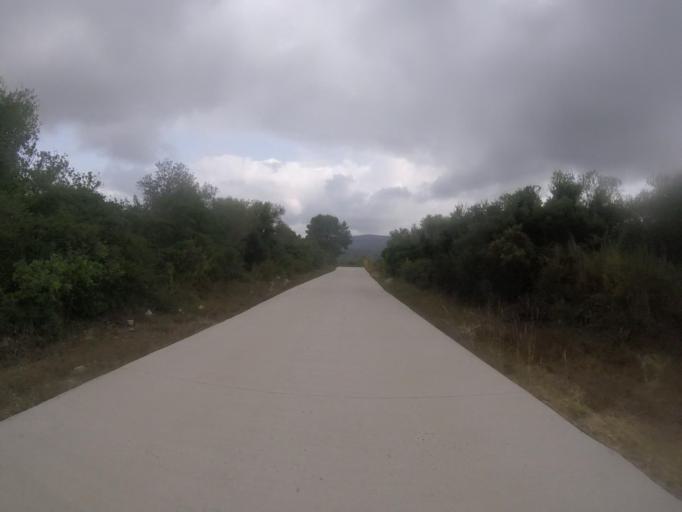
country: ES
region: Valencia
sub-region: Provincia de Castello
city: Santa Magdalena de Pulpis
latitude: 40.3380
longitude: 0.2758
